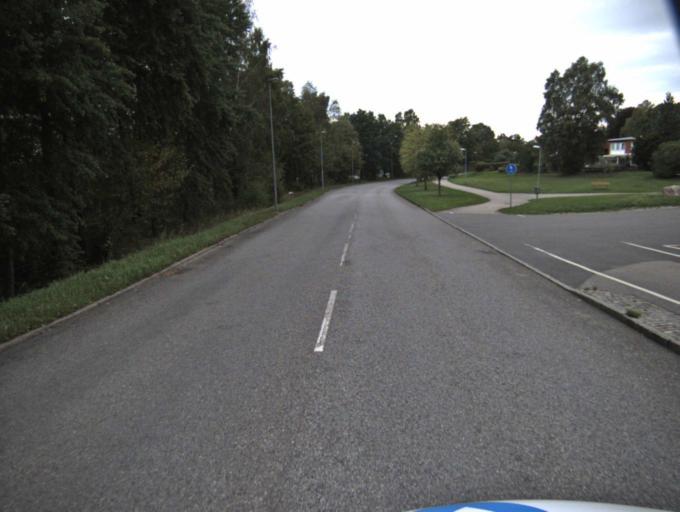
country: SE
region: Vaestra Goetaland
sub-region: Ulricehamns Kommun
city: Ulricehamn
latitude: 57.7803
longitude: 13.4135
